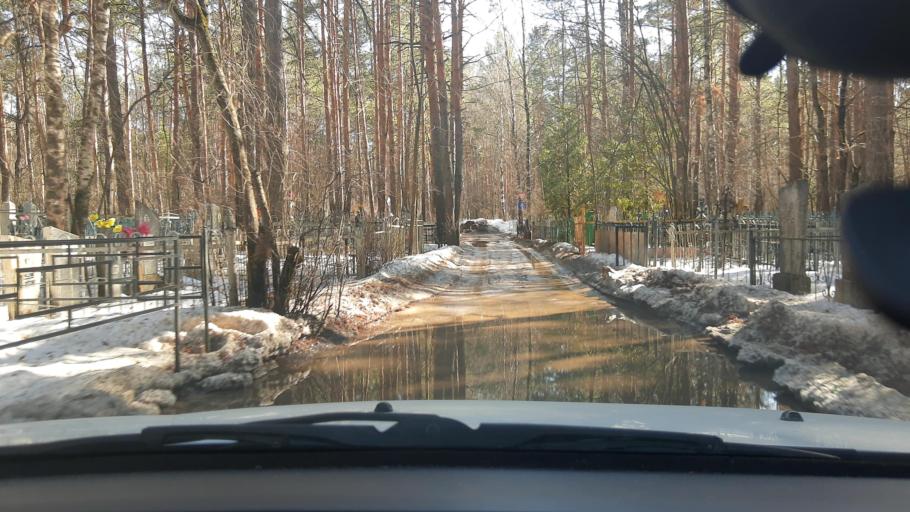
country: RU
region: Nizjnij Novgorod
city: Pyra
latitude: 56.2413
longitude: 43.3687
